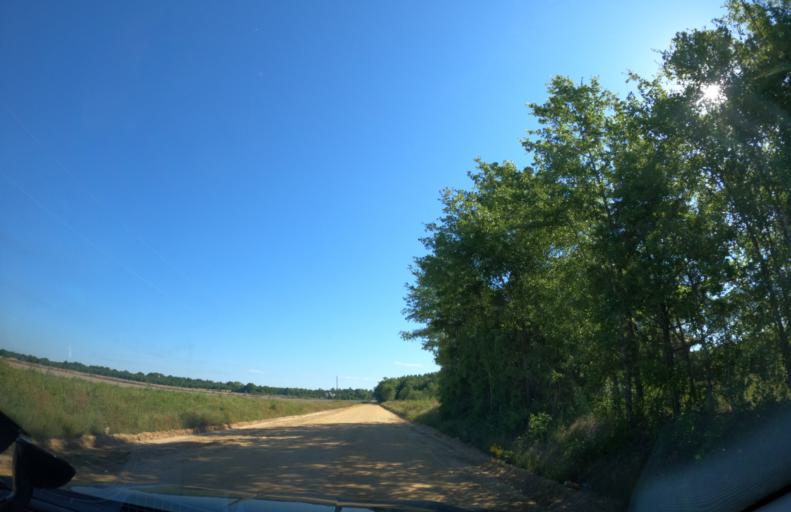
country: US
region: Georgia
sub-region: Jefferson County
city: Wrens
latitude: 33.2126
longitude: -82.3594
